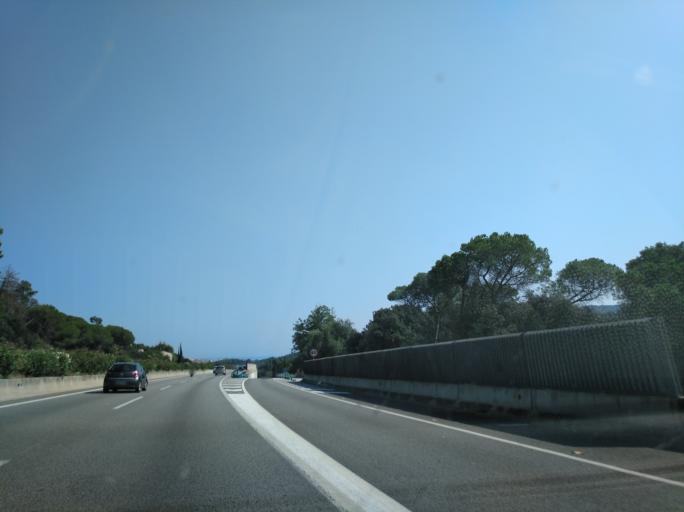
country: ES
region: Catalonia
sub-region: Provincia de Barcelona
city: Argentona
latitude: 41.5772
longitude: 2.3834
